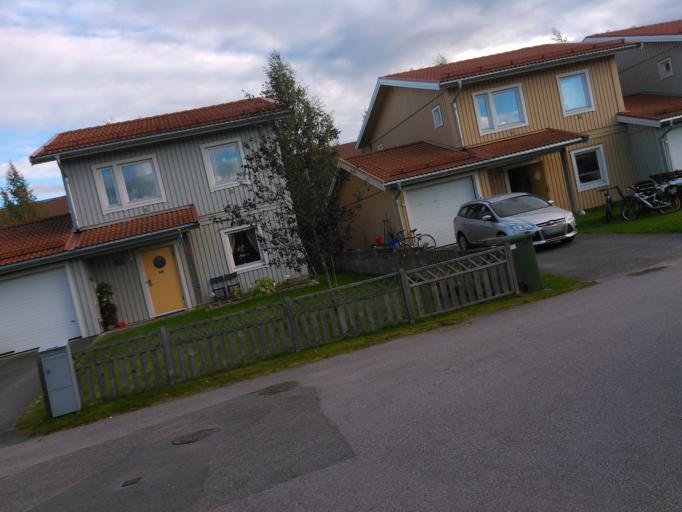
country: SE
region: Vaesterbotten
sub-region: Umea Kommun
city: Ersmark
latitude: 63.8055
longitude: 20.3411
